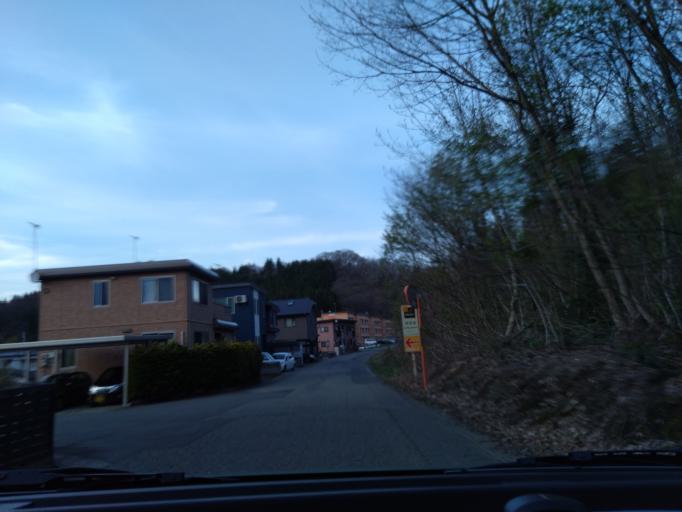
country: JP
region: Akita
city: Kakunodatemachi
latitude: 39.5921
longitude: 140.5789
